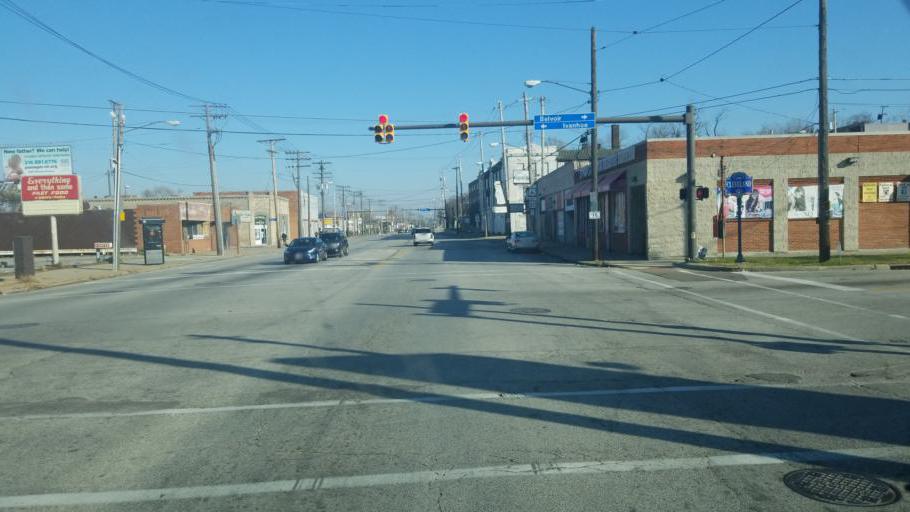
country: US
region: Ohio
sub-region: Cuyahoga County
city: East Cleveland
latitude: 41.5461
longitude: -81.5657
